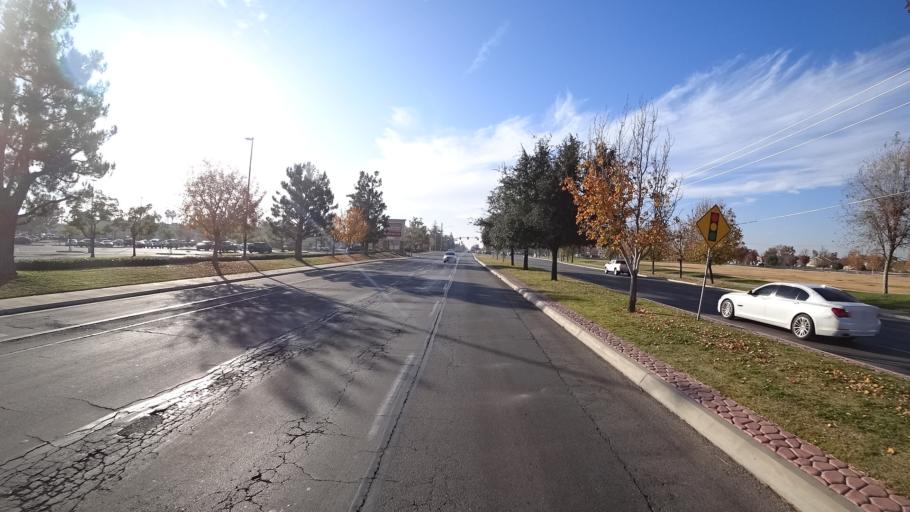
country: US
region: California
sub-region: Kern County
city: Greenacres
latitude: 35.3998
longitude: -119.1099
